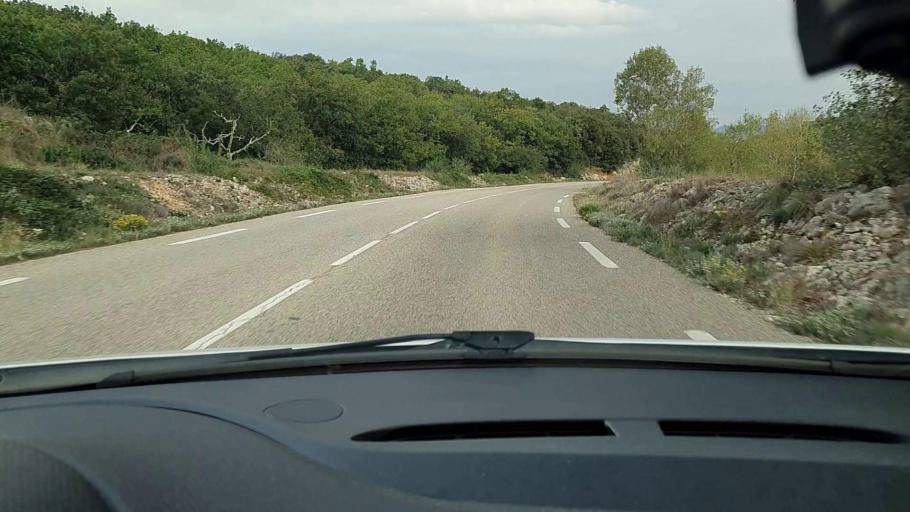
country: FR
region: Languedoc-Roussillon
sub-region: Departement du Gard
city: Barjac
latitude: 44.2264
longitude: 4.3183
